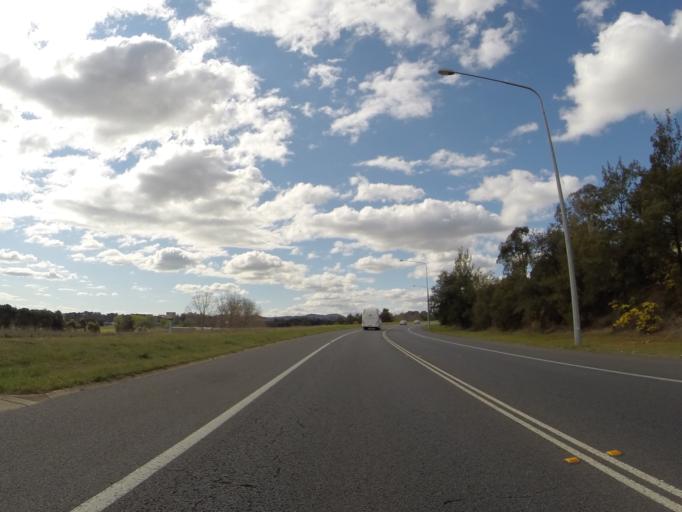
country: AU
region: Australian Capital Territory
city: Belconnen
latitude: -35.2057
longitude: 149.0897
